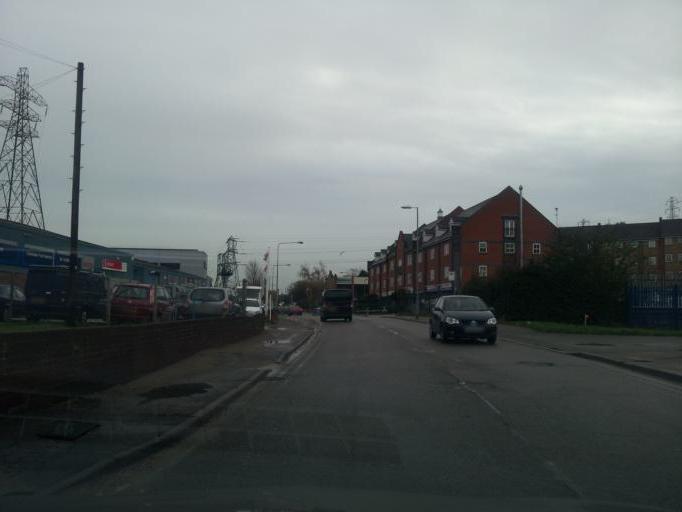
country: GB
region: England
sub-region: Essex
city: Colchester
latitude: 51.8785
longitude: 0.9282
